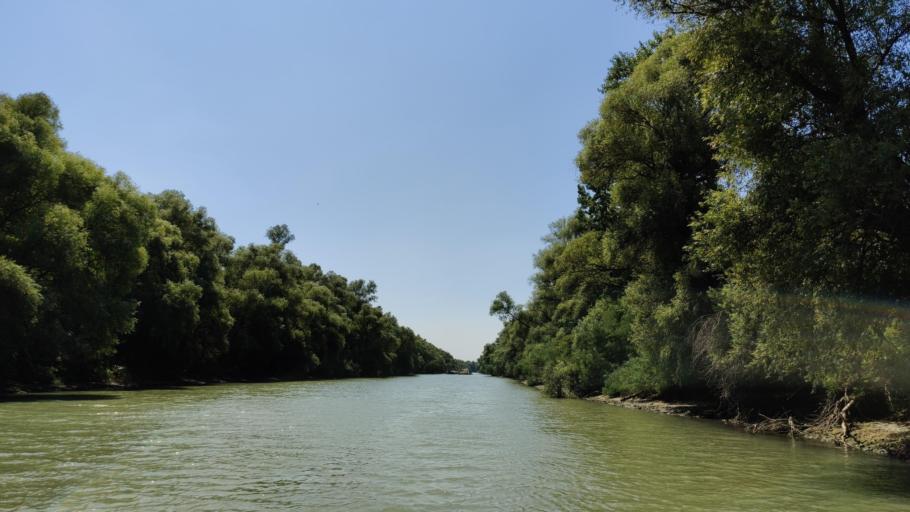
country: RO
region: Tulcea
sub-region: Comuna Pardina
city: Pardina
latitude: 45.2483
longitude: 28.9236
